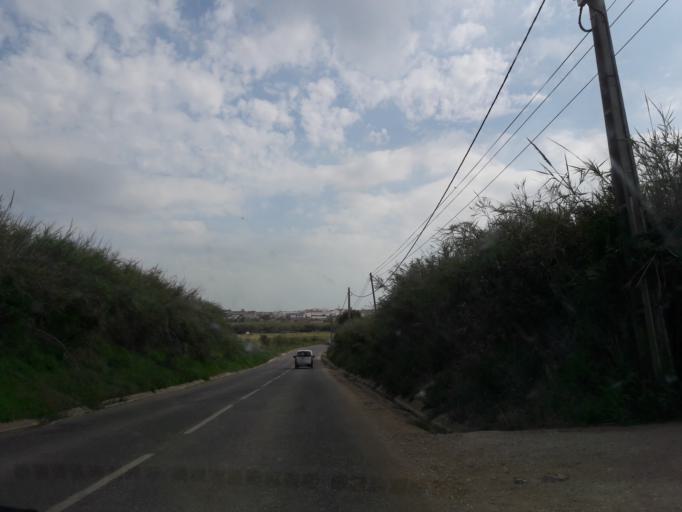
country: PT
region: Leiria
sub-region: Peniche
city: Atouguia da Baleia
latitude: 39.3485
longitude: -9.3239
